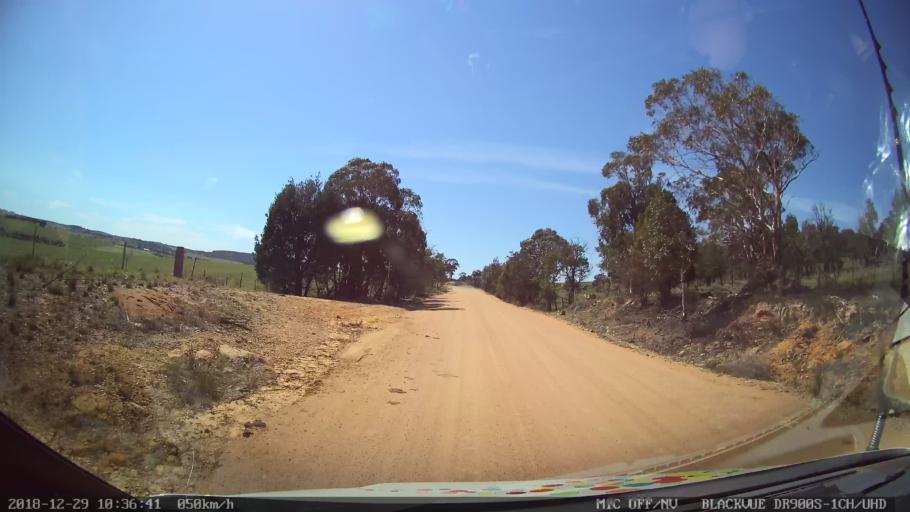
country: AU
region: New South Wales
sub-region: Yass Valley
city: Gundaroo
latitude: -34.9951
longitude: 149.4924
